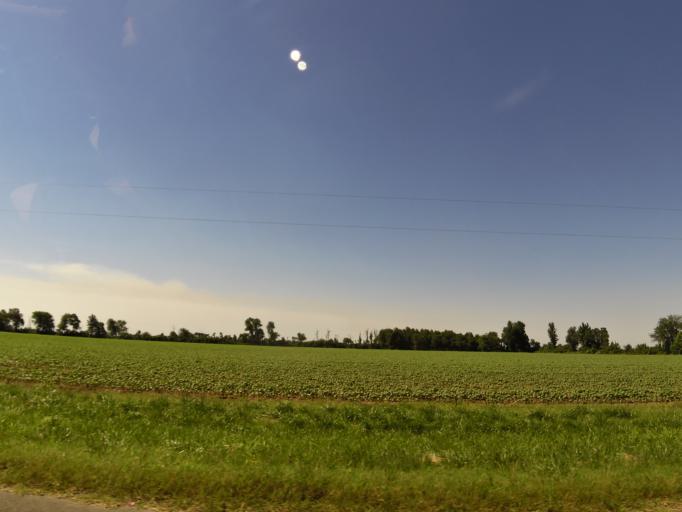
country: US
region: Missouri
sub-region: Dunklin County
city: Clarkton
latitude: 36.4984
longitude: -89.9844
